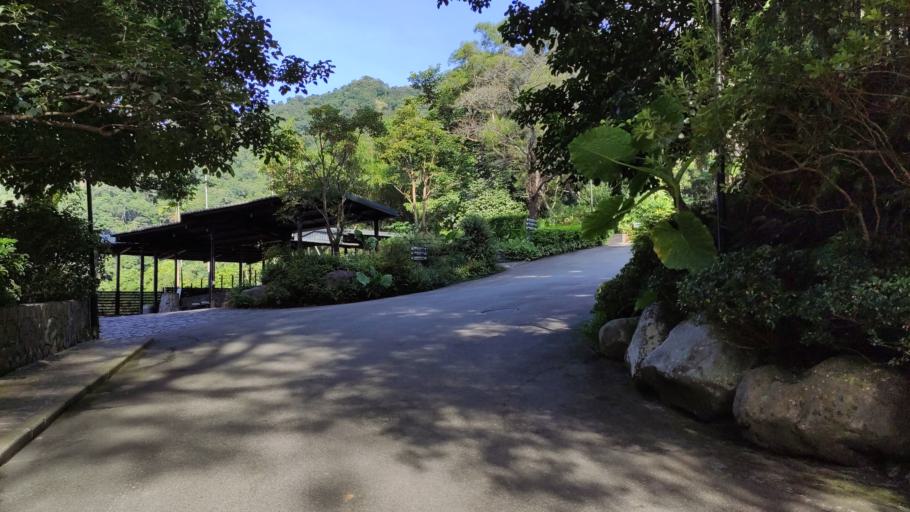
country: TW
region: Taiwan
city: Daxi
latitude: 24.8721
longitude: 121.4076
